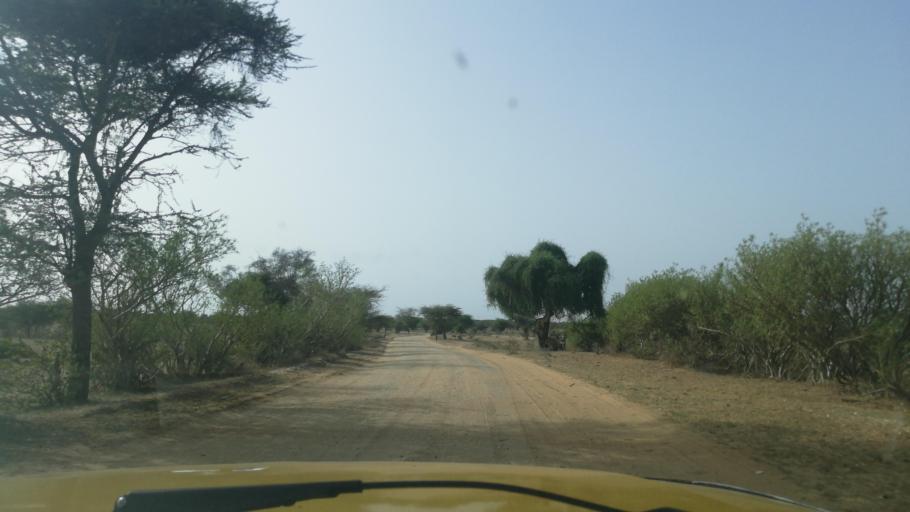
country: SN
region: Saint-Louis
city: Saint-Louis
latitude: 16.0575
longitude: -16.3324
